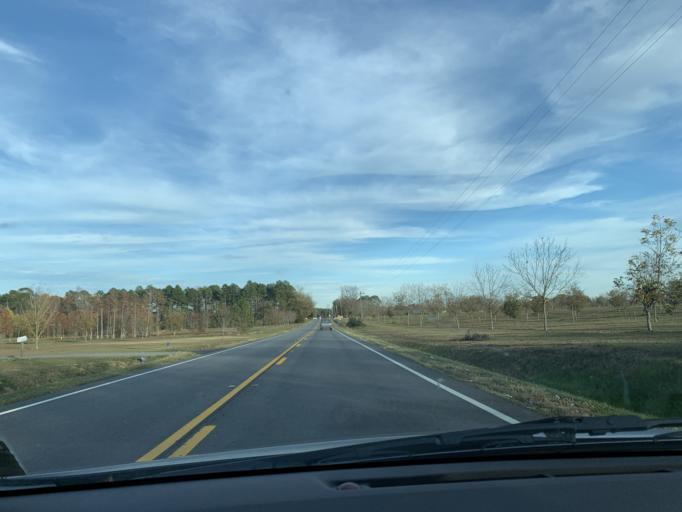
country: US
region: Georgia
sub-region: Irwin County
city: Ocilla
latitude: 31.5927
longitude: -83.2177
